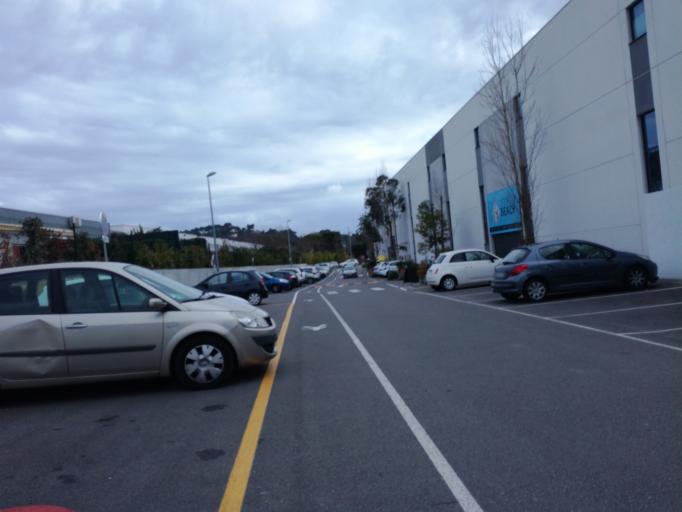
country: FR
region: Provence-Alpes-Cote d'Azur
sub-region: Departement des Alpes-Maritimes
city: Mouans-Sartoux
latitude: 43.6122
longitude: 6.9726
